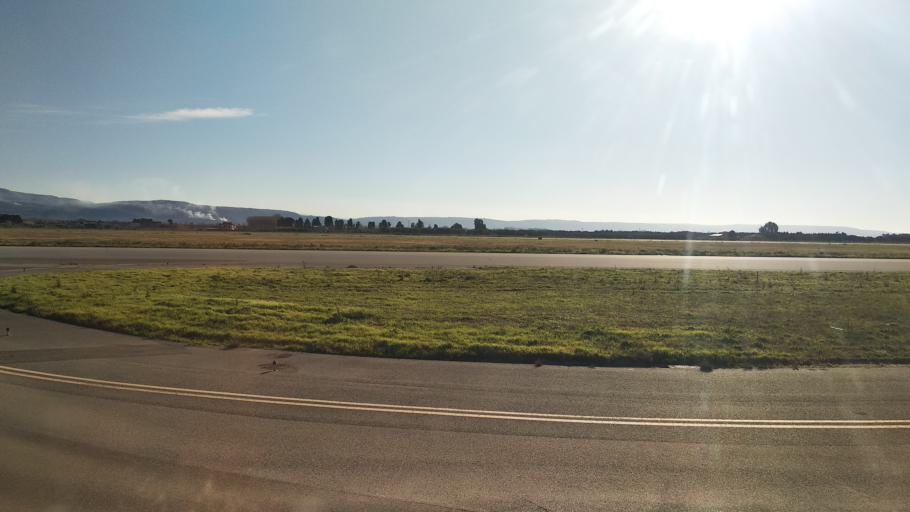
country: IT
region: Calabria
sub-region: Provincia di Catanzaro
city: Santa Eufemia Lamezia
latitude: 38.9080
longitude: 16.2453
